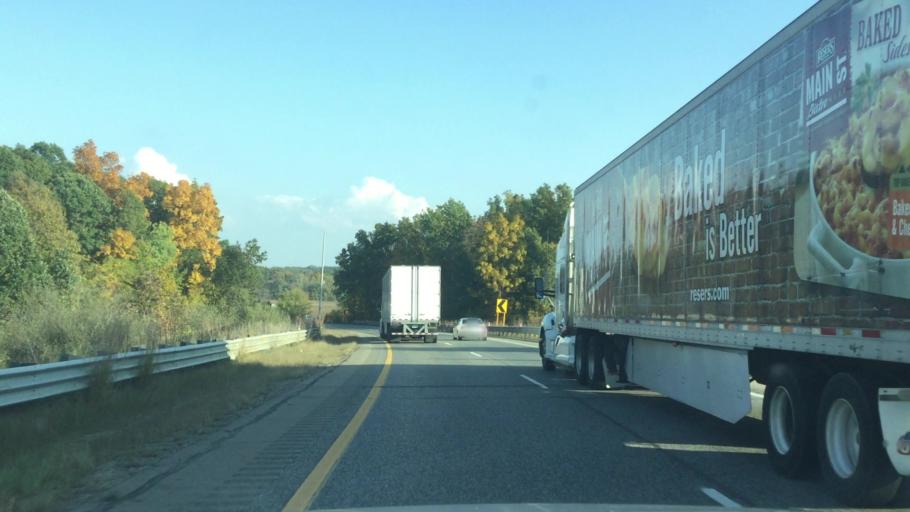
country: US
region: Michigan
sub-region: Washtenaw County
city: Chelsea
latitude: 42.2926
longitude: -84.0871
